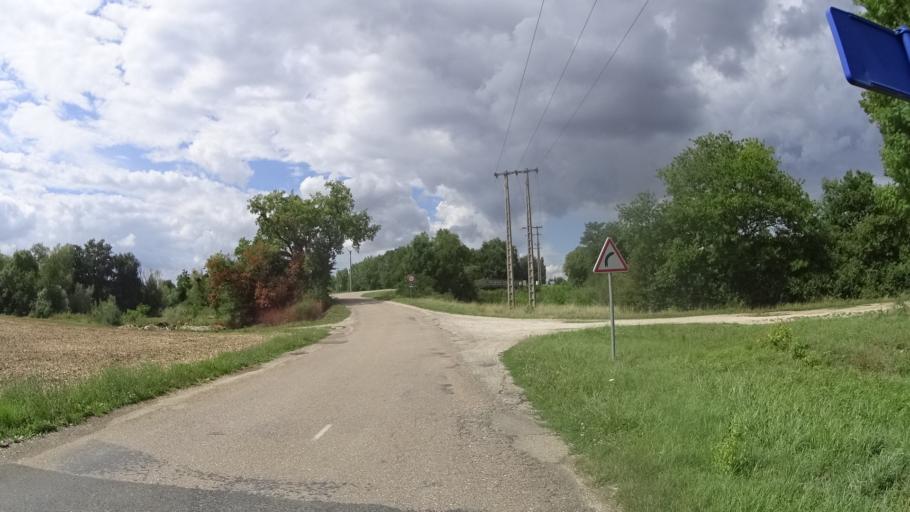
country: FR
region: Champagne-Ardenne
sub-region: Departement de la Haute-Marne
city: Villiers-en-Lieu
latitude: 48.6508
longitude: 4.8293
